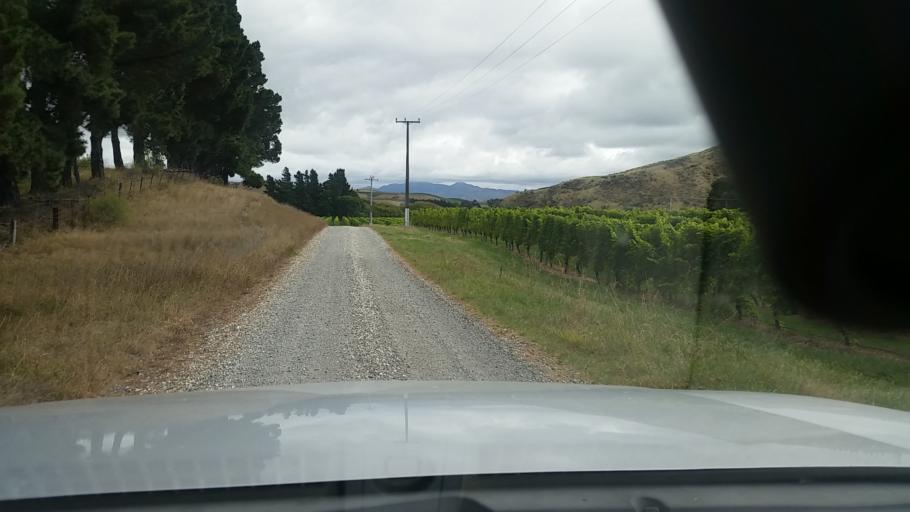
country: NZ
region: Marlborough
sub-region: Marlborough District
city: Blenheim
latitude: -41.6869
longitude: 174.1294
